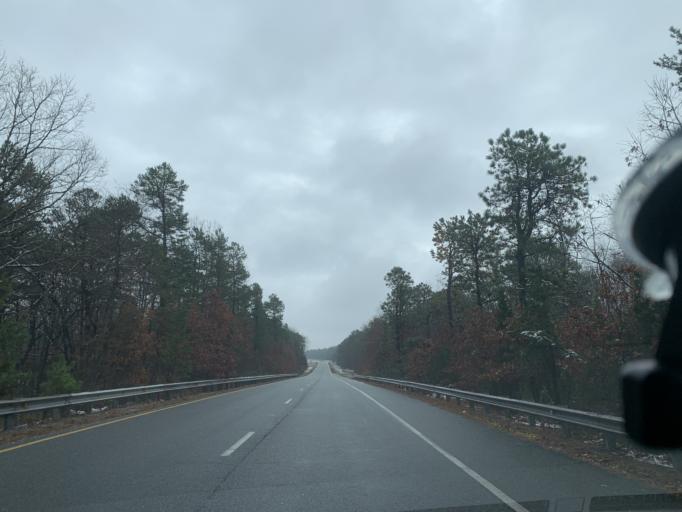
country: US
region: New Jersey
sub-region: Atlantic County
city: Pomona
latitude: 39.4492
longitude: -74.6253
